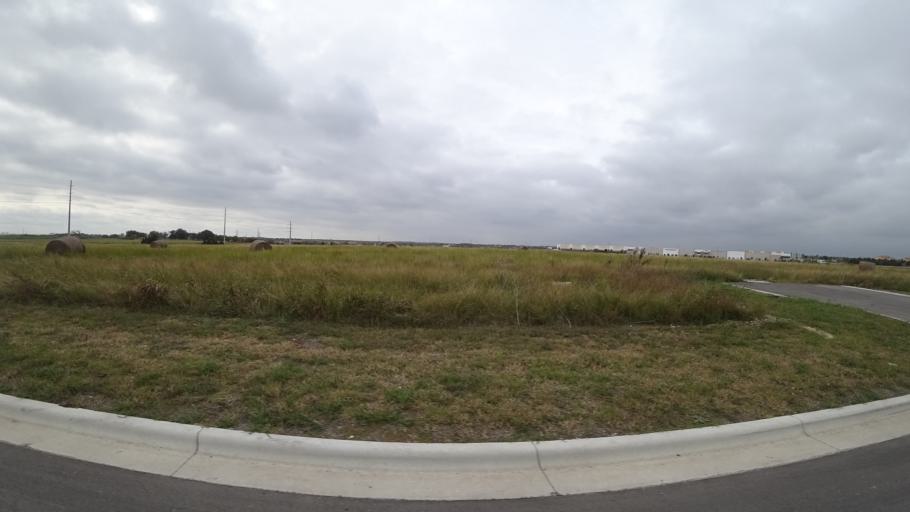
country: US
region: Texas
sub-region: Travis County
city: Pflugerville
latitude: 30.4216
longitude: -97.5840
